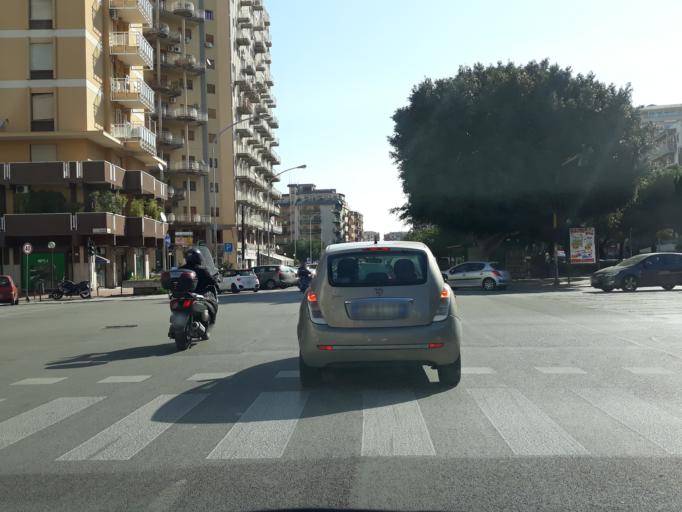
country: IT
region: Sicily
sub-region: Palermo
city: Palermo
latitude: 38.1287
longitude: 13.3352
